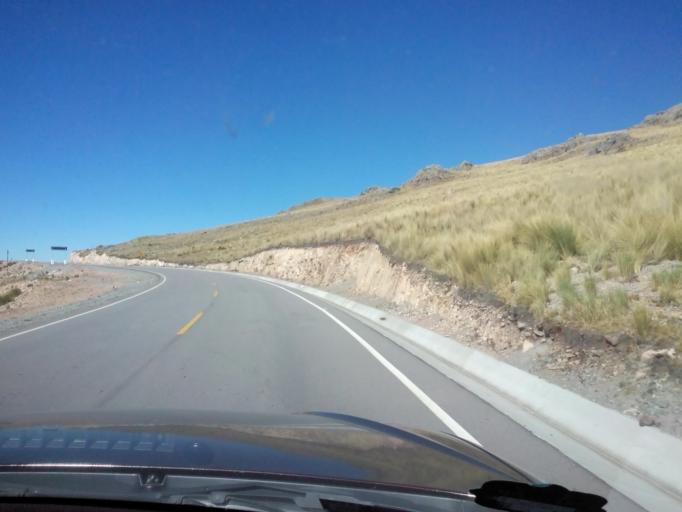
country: PE
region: Ayacucho
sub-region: Provincia de Huamanga
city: Acocro
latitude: -13.3696
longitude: -74.0810
